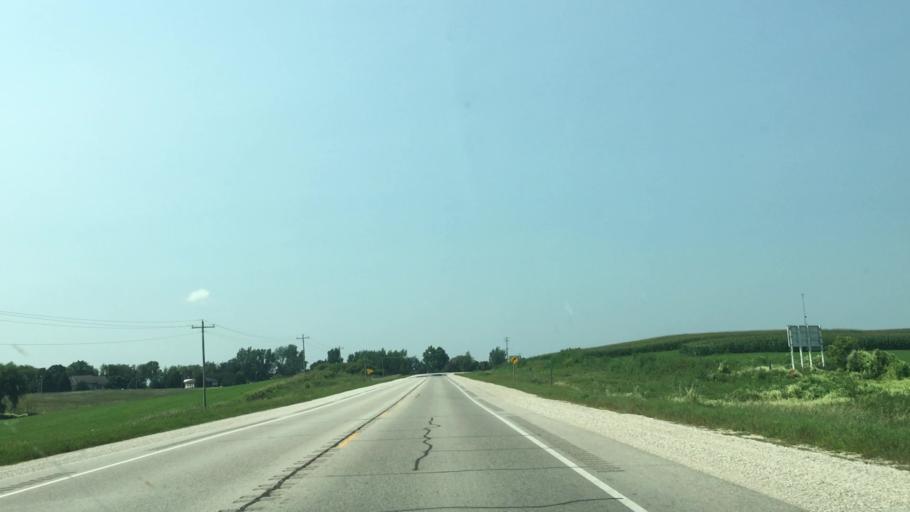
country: US
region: Iowa
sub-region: Winneshiek County
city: Decorah
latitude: 43.1920
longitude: -91.8687
